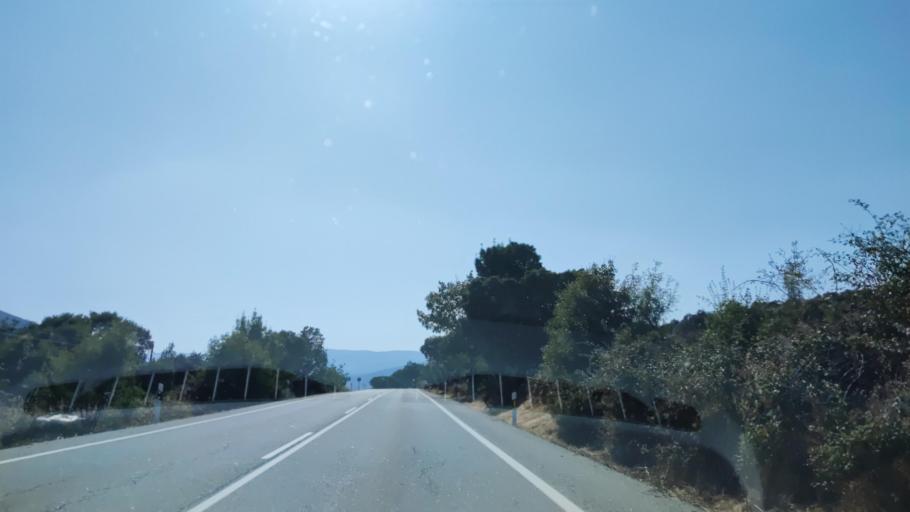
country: ES
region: Madrid
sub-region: Provincia de Madrid
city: Lozoya
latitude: 40.9469
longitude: -3.7512
